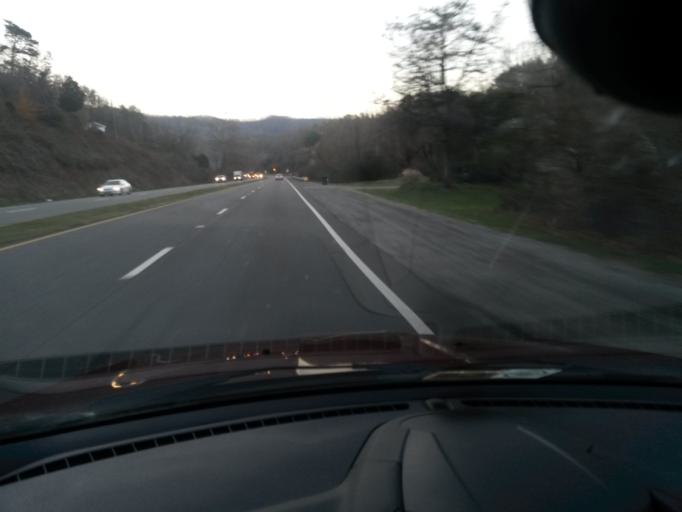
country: US
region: Virginia
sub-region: Roanoke County
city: Narrows
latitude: 37.1897
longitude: -79.9363
